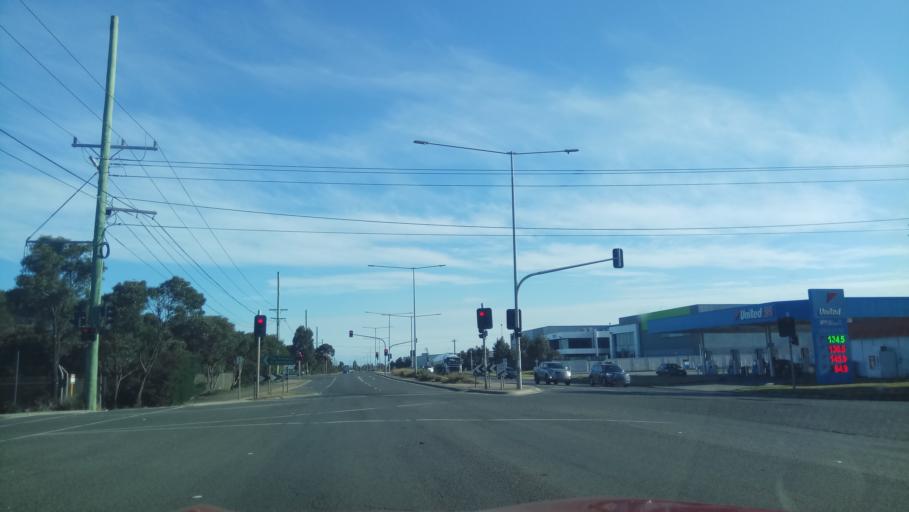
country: AU
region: Victoria
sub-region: Hobsons Bay
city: Altona North
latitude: -37.8386
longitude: 144.8258
